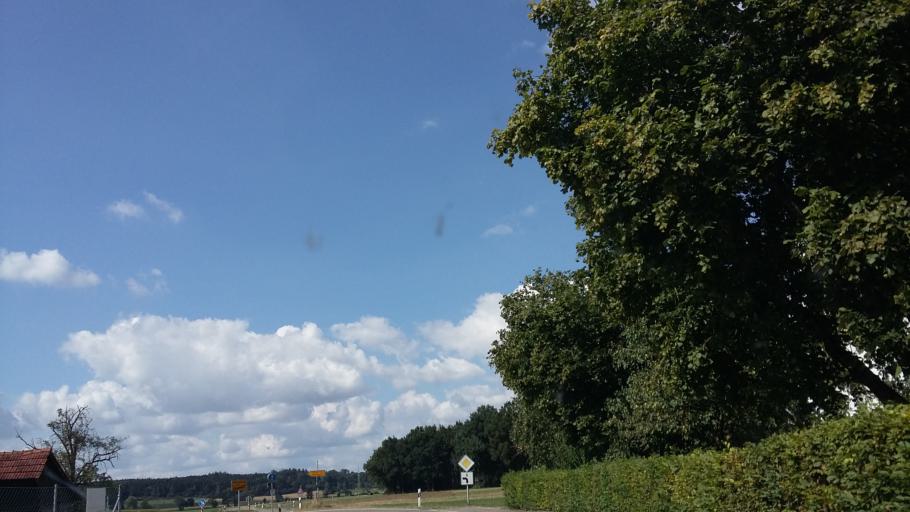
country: DE
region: Bavaria
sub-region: Swabia
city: Holzheim
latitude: 48.3547
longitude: 10.1139
